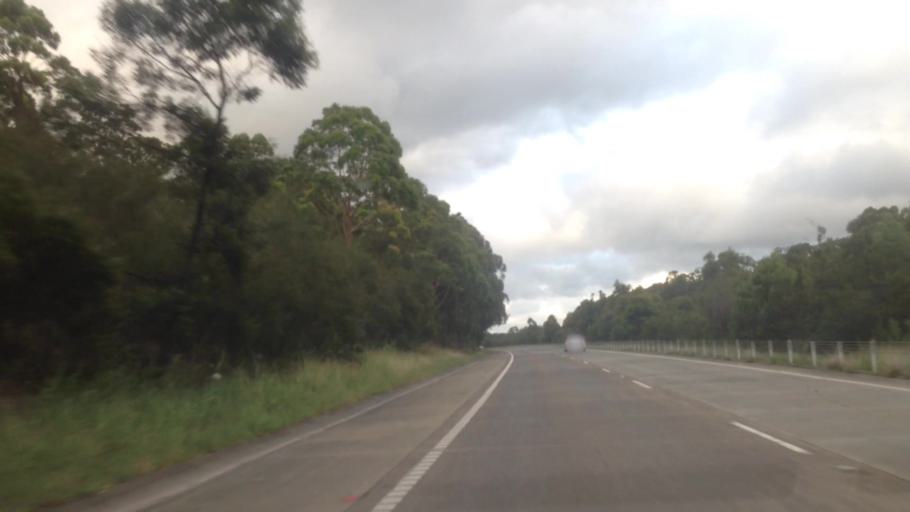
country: AU
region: New South Wales
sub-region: Wyong Shire
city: Charmhaven
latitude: -33.2008
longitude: 151.4617
